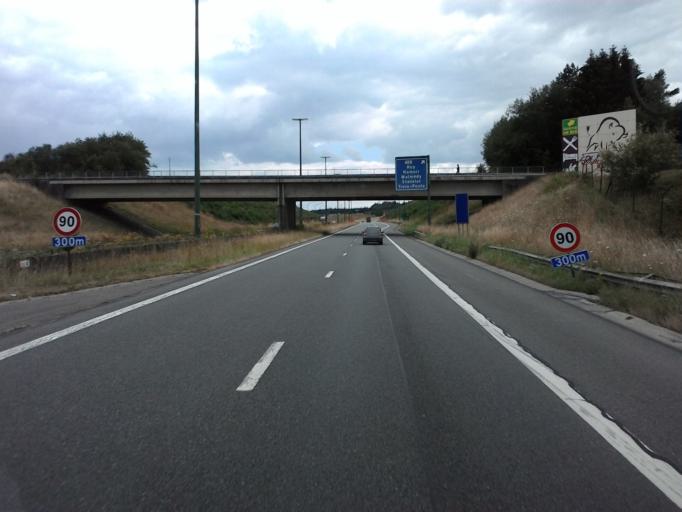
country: BE
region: Wallonia
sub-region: Province de Liege
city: Ferrieres
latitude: 50.3891
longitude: 5.6842
